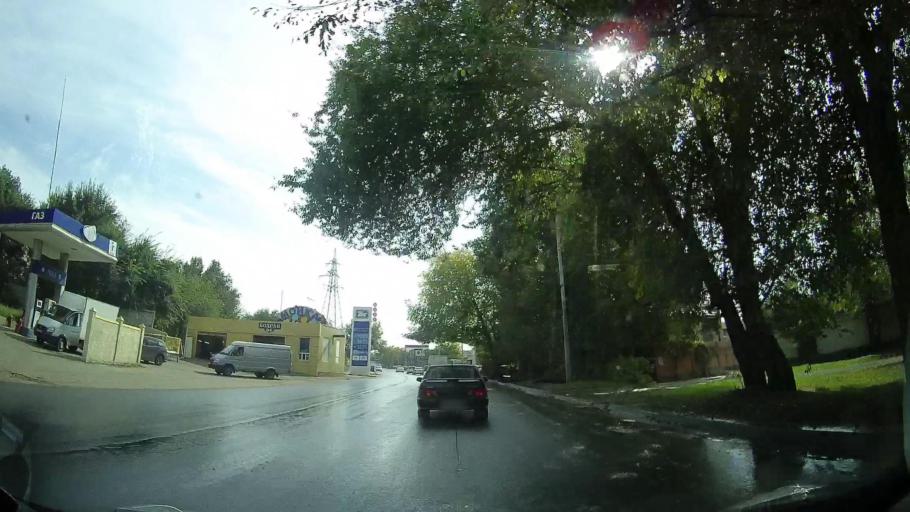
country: RU
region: Rostov
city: Severnyy
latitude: 47.2748
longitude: 39.7048
